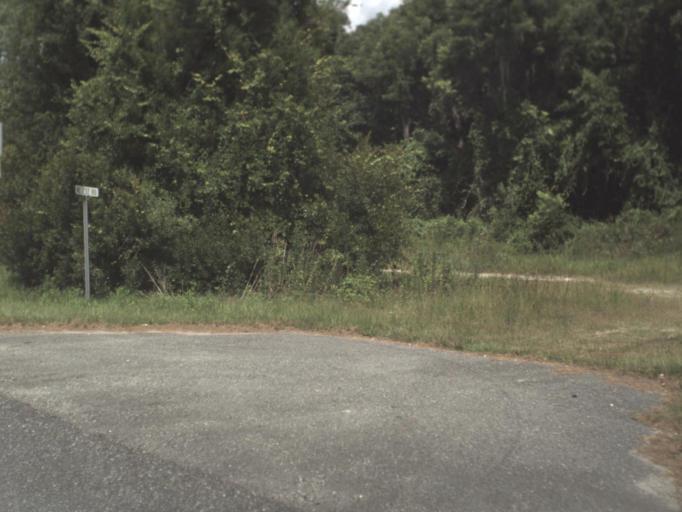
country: US
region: Florida
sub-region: Union County
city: Lake Butler
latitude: 30.0705
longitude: -82.2243
